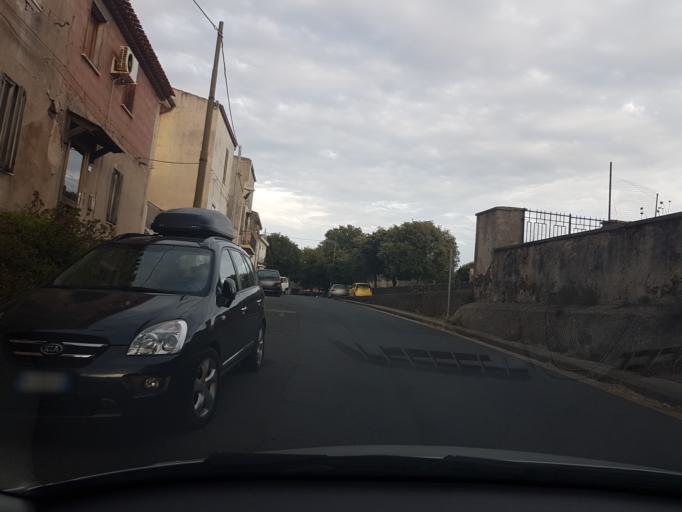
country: IT
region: Sardinia
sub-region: Provincia di Oristano
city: Seneghe
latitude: 40.0824
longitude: 8.6084
